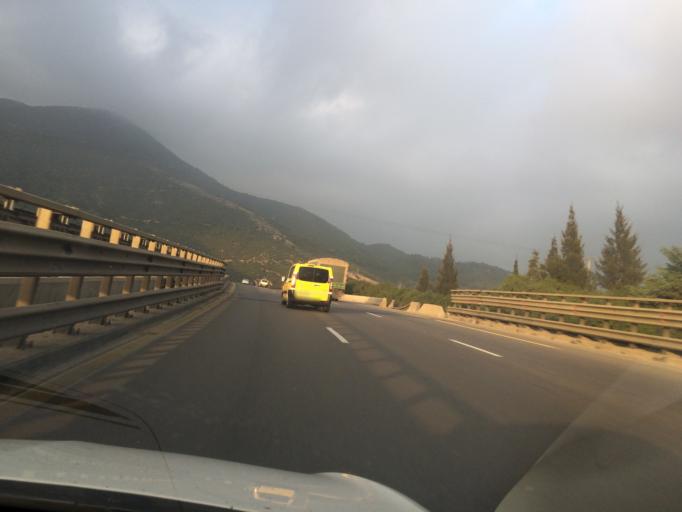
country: DZ
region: Tipaza
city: El Affroun
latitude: 36.3980
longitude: 2.5378
